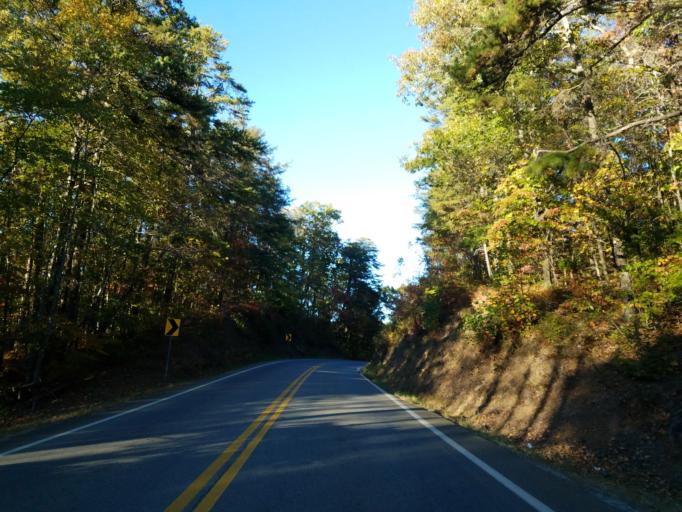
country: US
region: Georgia
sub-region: Dawson County
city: Dawsonville
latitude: 34.4277
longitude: -84.2204
